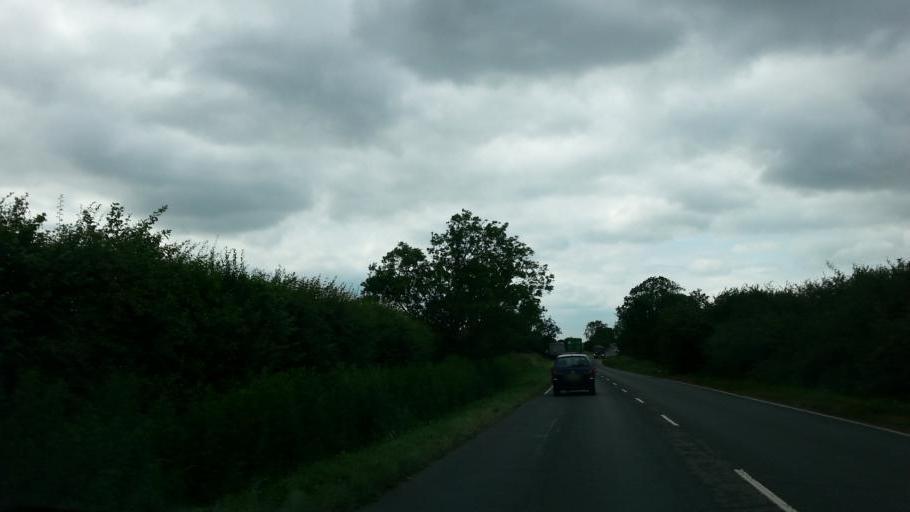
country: GB
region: England
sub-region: Cambridgeshire
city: Godmanchester
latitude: 52.3026
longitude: -0.1582
